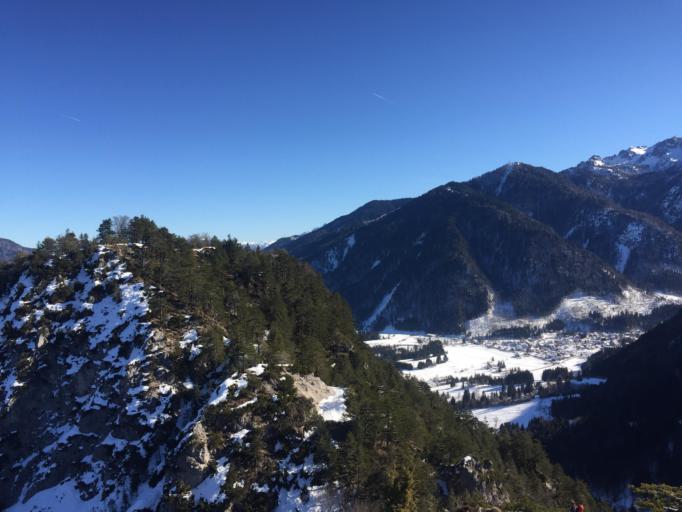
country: IT
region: Friuli Venezia Giulia
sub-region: Provincia di Udine
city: Malborghetto
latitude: 46.5026
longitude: 13.4680
